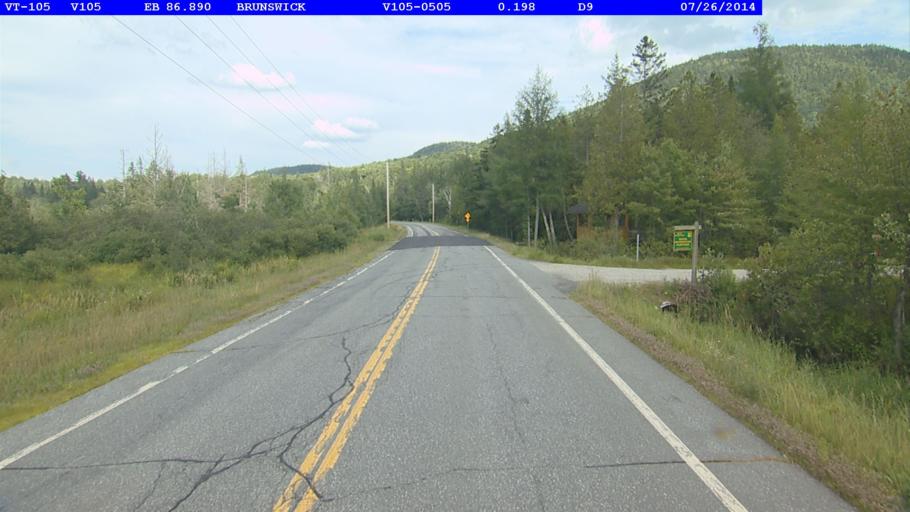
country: US
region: New Hampshire
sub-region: Coos County
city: Stratford
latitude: 44.7604
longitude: -71.7150
